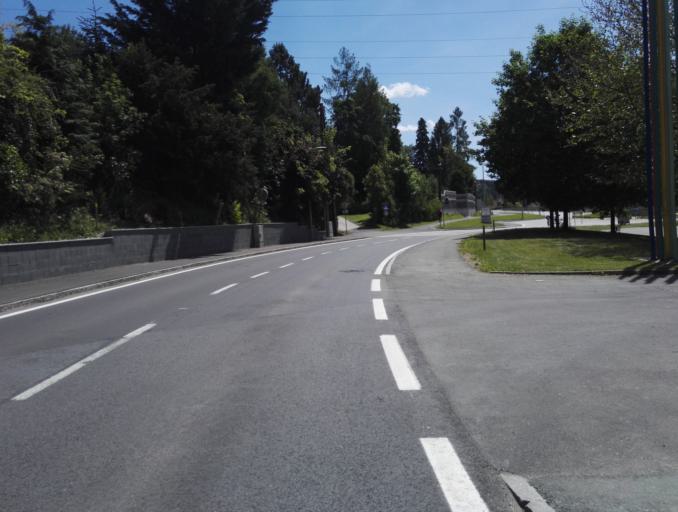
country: AT
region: Styria
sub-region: Politischer Bezirk Graz-Umgebung
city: Grambach
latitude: 47.0198
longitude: 15.5020
